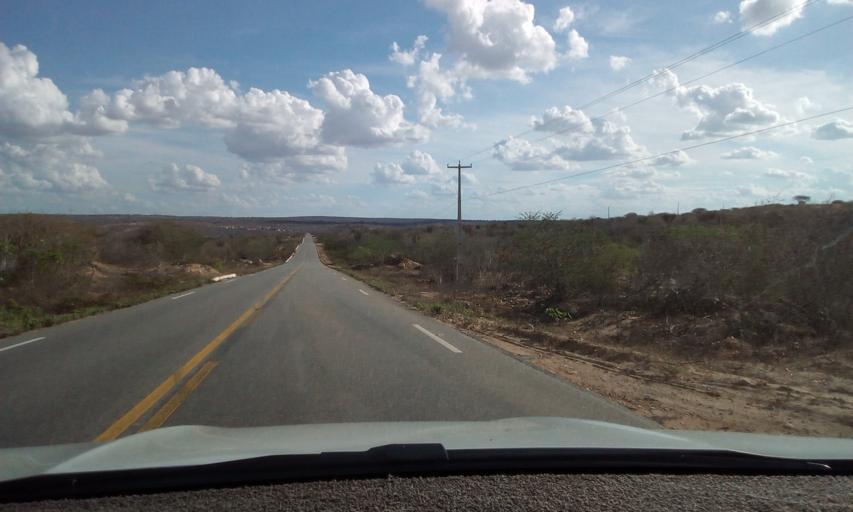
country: BR
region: Paraiba
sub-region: Soledade
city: Soledade
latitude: -6.8355
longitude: -36.4067
